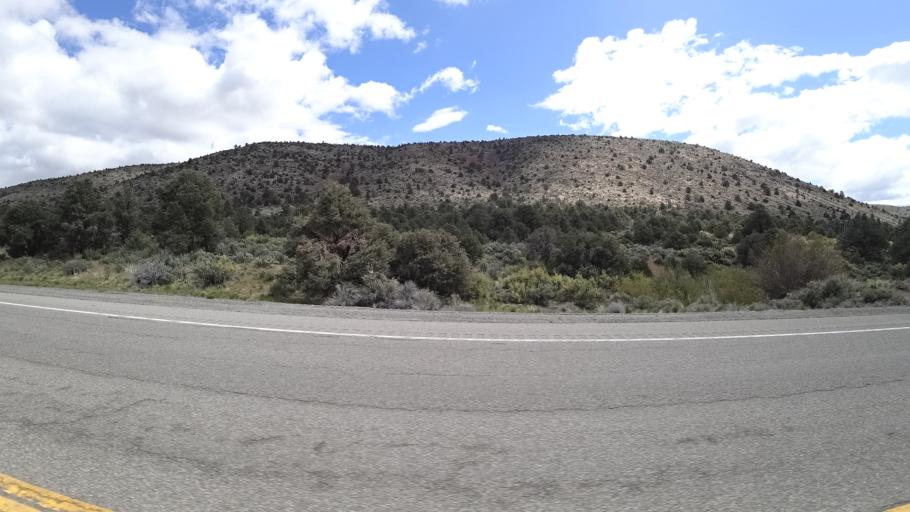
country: US
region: Nevada
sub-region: Douglas County
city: Gardnerville Ranchos
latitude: 38.7614
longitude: -119.5764
